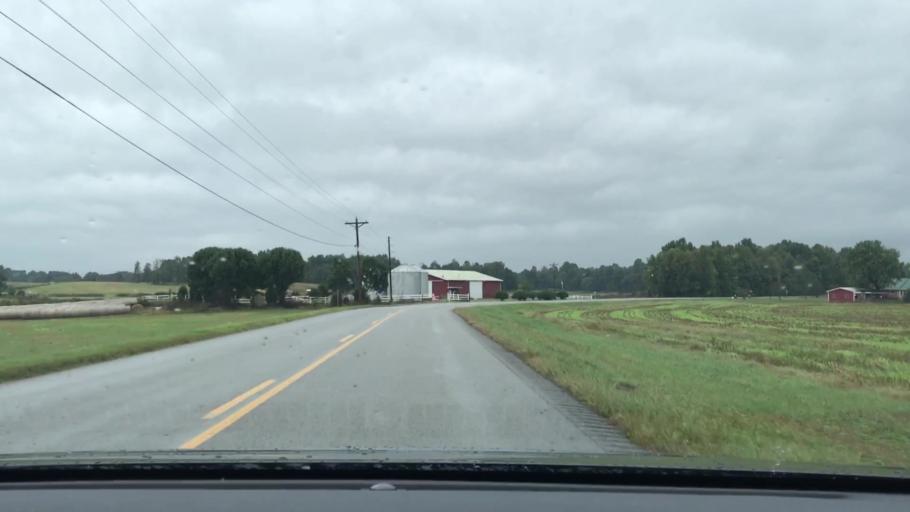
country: US
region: Kentucky
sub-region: McLean County
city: Calhoun
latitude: 37.4541
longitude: -87.2350
